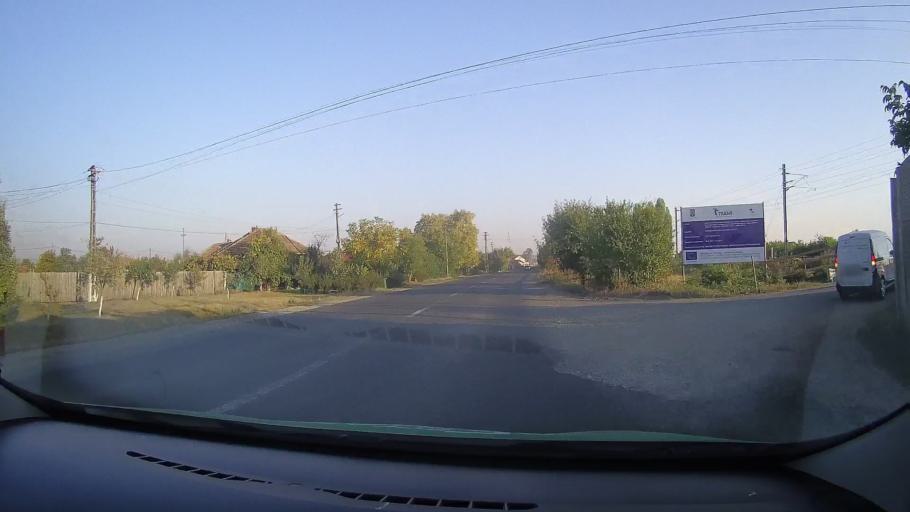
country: RO
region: Arad
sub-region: Comuna Sofronea
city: Sofronea
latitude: 46.2734
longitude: 21.3149
